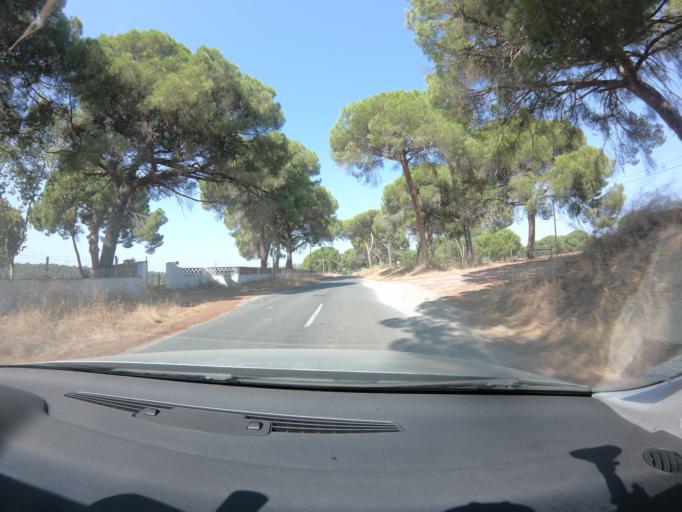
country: PT
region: Setubal
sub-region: Alcacer do Sal
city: Alcacer do Sal
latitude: 38.2807
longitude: -8.3969
